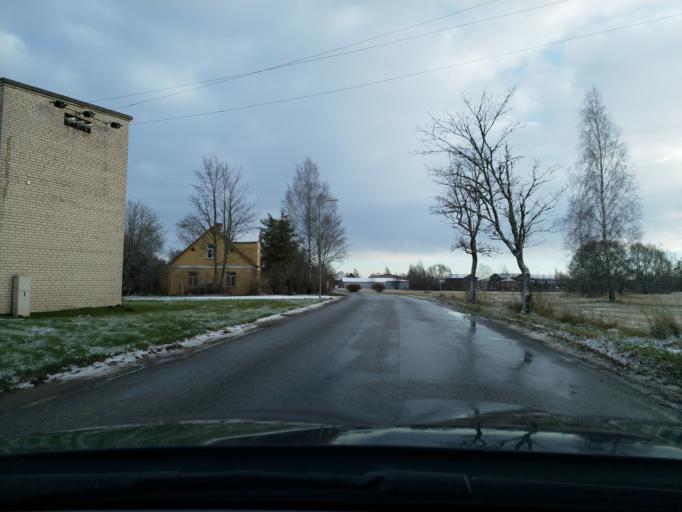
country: LV
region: Kuldigas Rajons
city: Kuldiga
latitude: 56.9609
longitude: 21.9862
